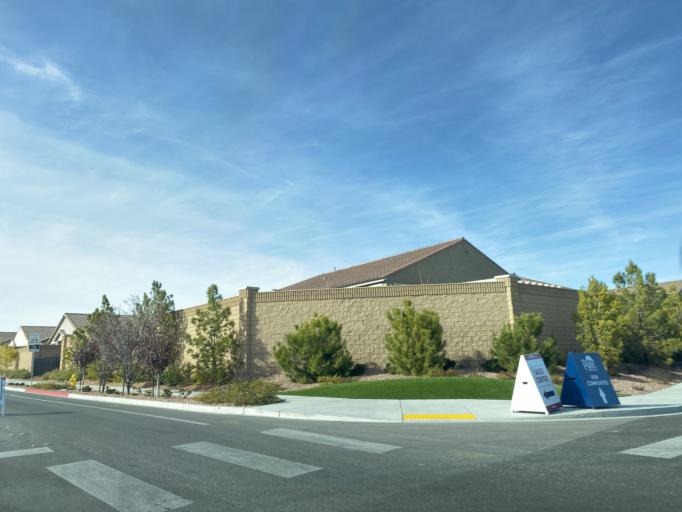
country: US
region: Nevada
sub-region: Clark County
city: Summerlin South
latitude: 36.3106
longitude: -115.3214
